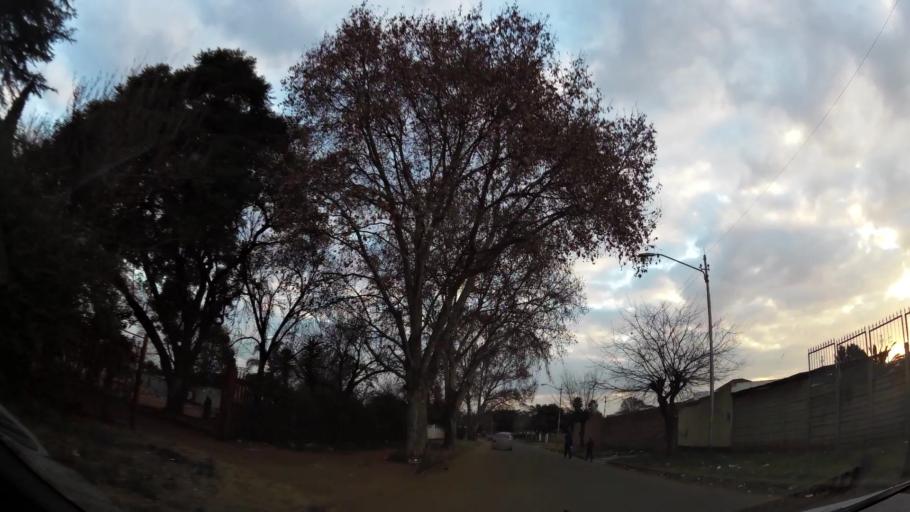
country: ZA
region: Gauteng
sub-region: Ekurhuleni Metropolitan Municipality
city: Germiston
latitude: -26.1912
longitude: 28.1619
